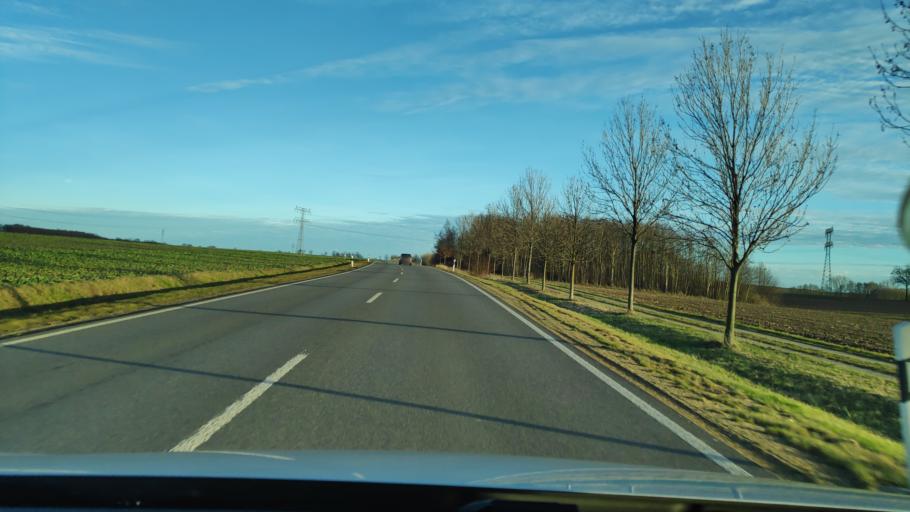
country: DE
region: Saxony
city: Zwickau
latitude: 50.7656
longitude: 12.5126
